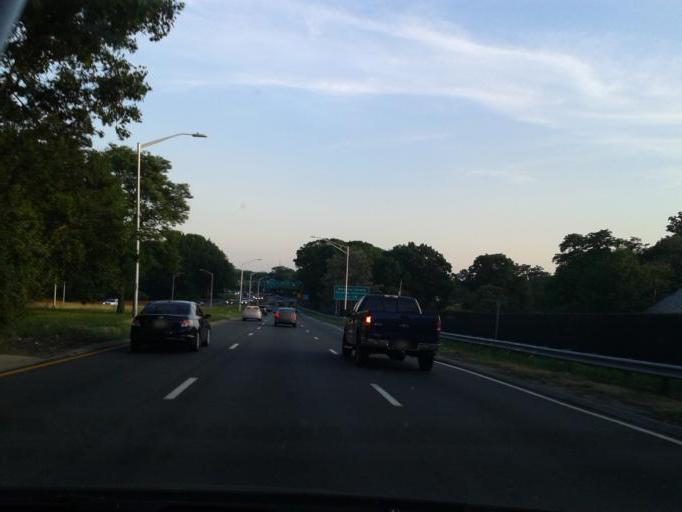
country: US
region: New York
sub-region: Bronx
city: The Bronx
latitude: 40.8614
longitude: -73.8724
